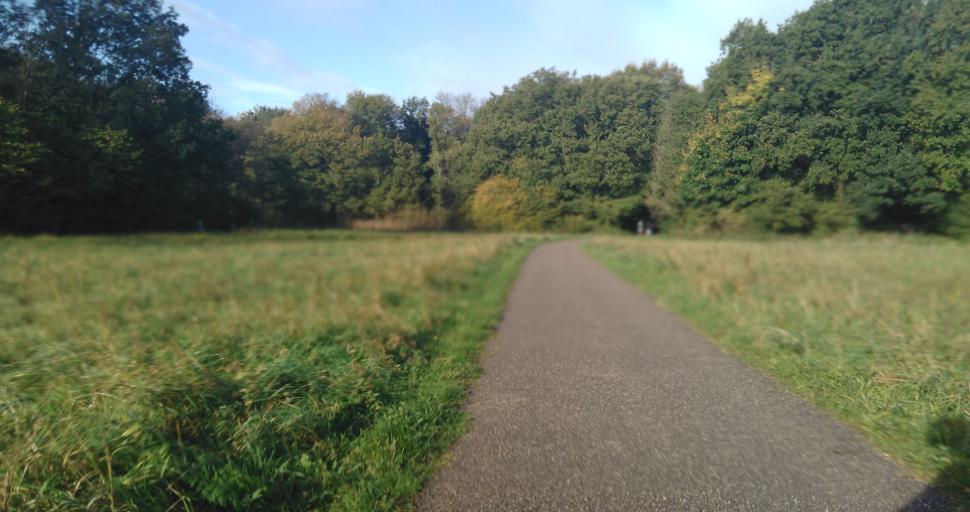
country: NL
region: North Holland
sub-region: Gemeente Amstelveen
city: Amstelveen
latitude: 52.3148
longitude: 4.8338
